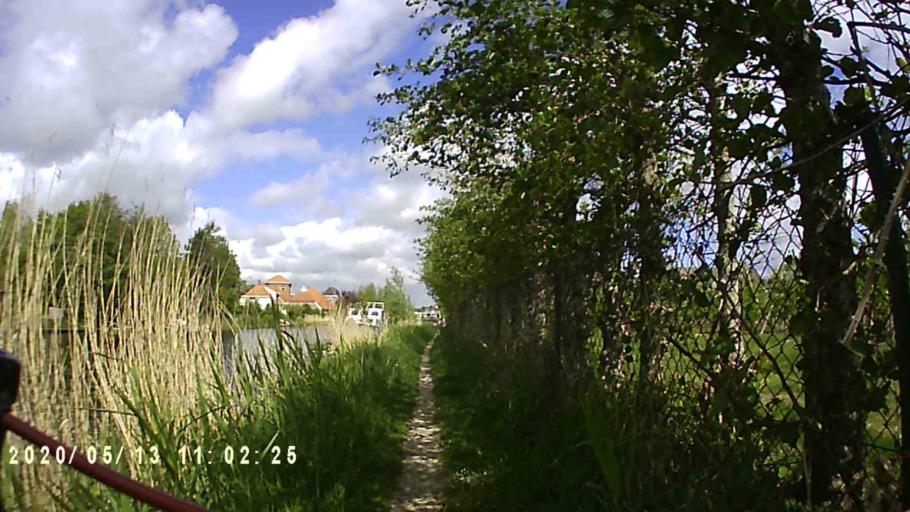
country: NL
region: Groningen
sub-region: Gemeente Zuidhorn
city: Grijpskerk
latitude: 53.2850
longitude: 6.3269
